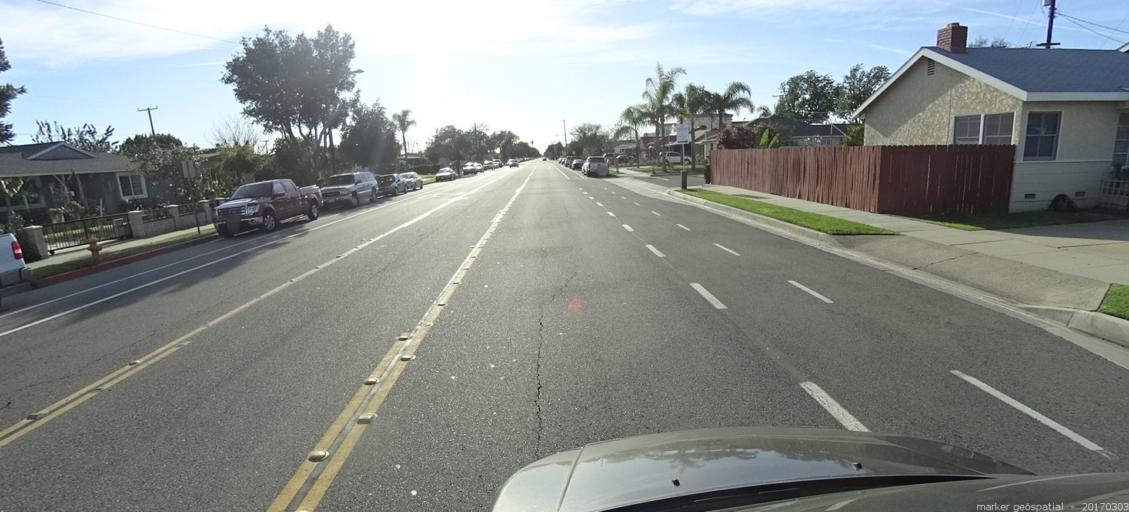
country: US
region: California
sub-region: Orange County
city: Anaheim
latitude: 33.8374
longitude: -117.8956
